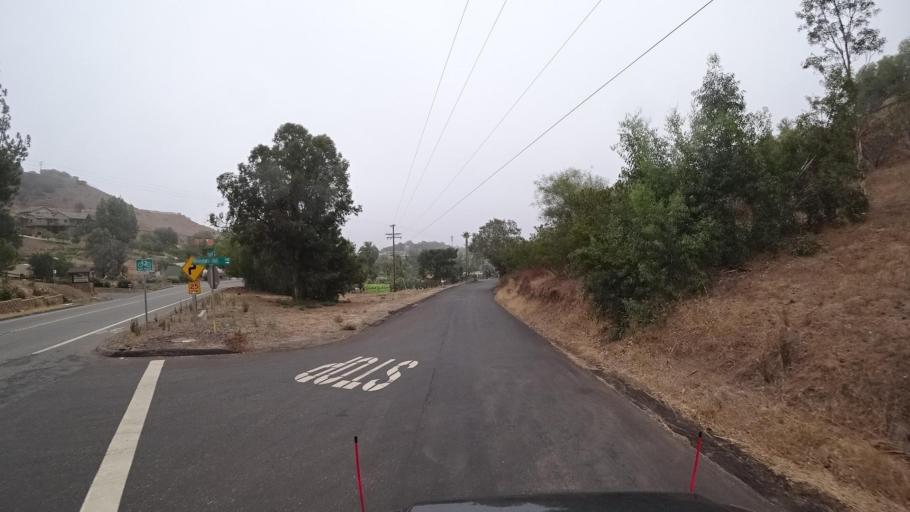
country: US
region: California
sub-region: San Diego County
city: Rainbow
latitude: 33.3904
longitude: -117.1844
